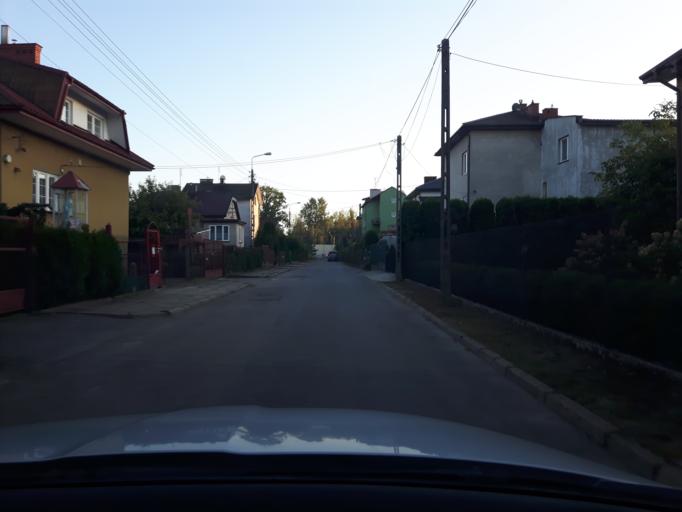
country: PL
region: Masovian Voivodeship
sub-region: Powiat wolominski
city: Kobylka
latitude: 52.3275
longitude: 21.1903
